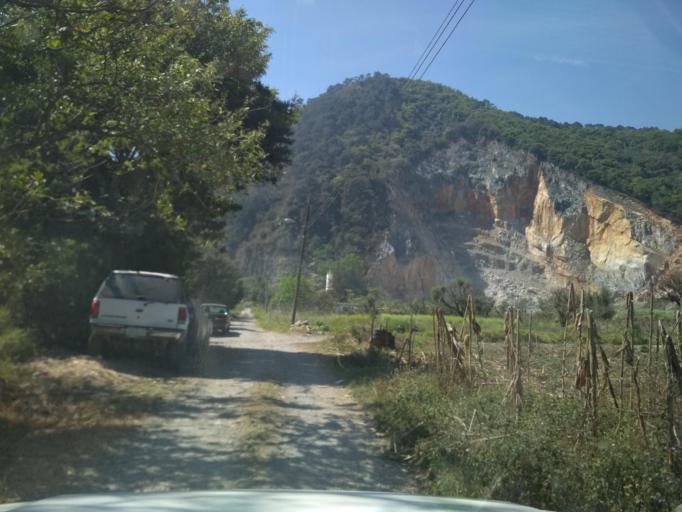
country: MX
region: Veracruz
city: Jalapilla
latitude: 18.8217
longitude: -97.0929
